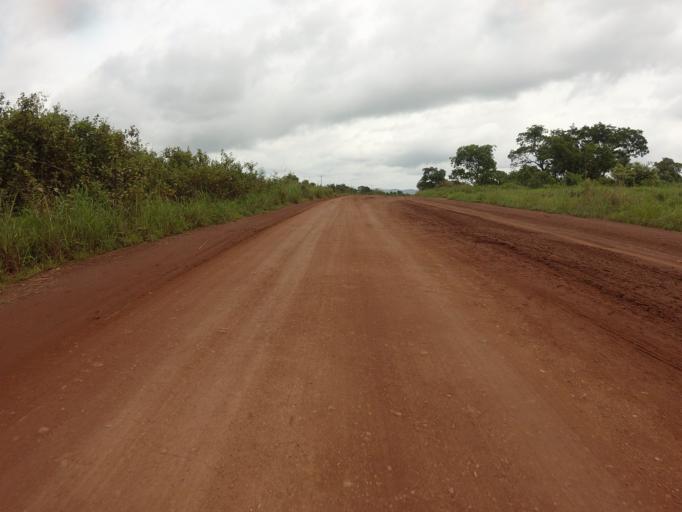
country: GH
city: Kpandae
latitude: 8.3108
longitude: 0.4832
